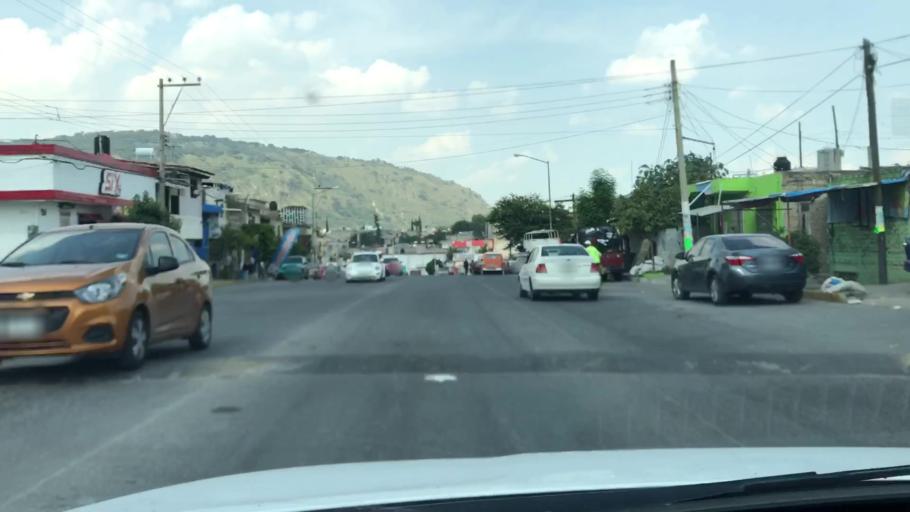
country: MX
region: Jalisco
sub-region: Tlajomulco de Zuniga
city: Palomar
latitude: 20.6358
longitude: -103.4603
